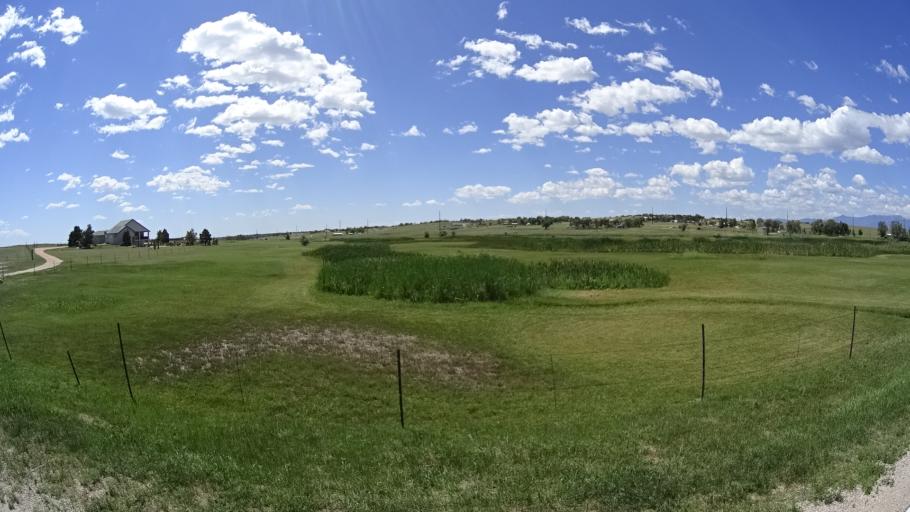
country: US
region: Colorado
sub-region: El Paso County
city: Cimarron Hills
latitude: 38.9261
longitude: -104.6045
